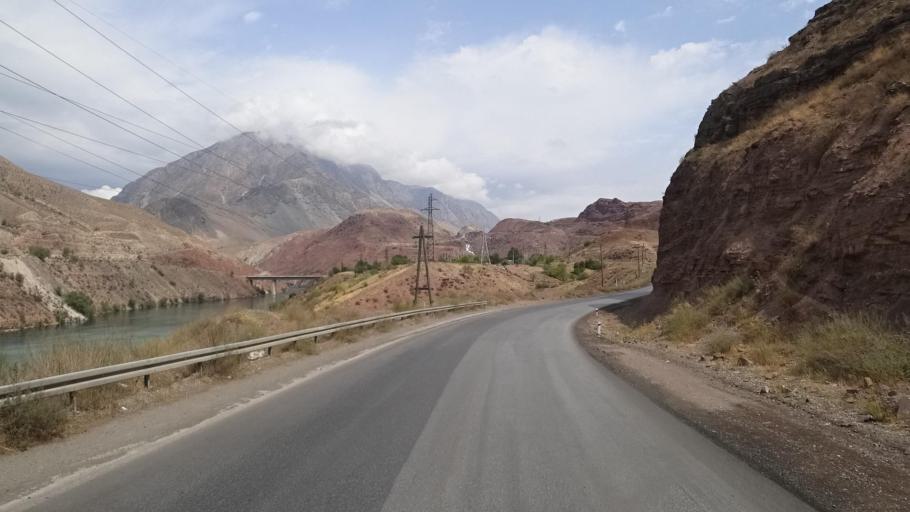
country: KG
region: Jalal-Abad
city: Toktogul
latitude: 41.6179
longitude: 72.6269
